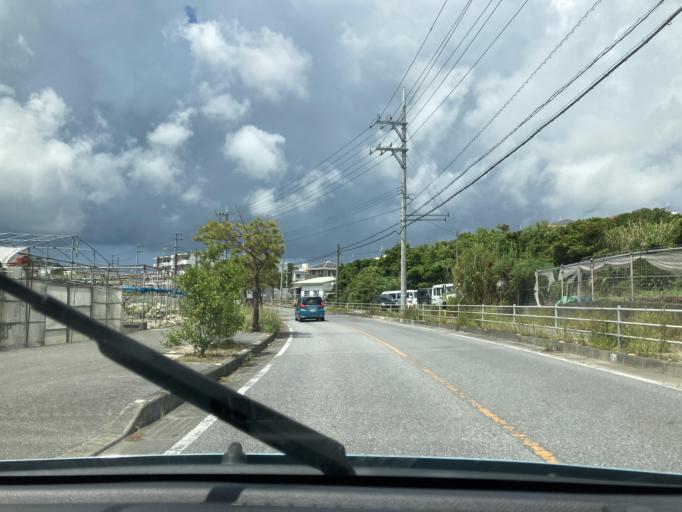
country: JP
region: Okinawa
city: Tomigusuku
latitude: 26.1748
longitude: 127.7510
